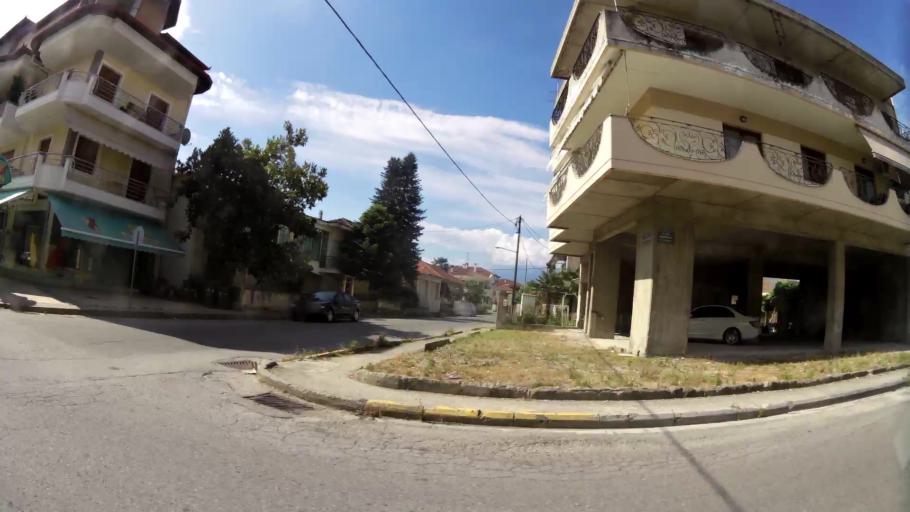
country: GR
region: Central Macedonia
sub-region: Nomos Pierias
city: Katerini
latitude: 40.2799
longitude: 22.4992
